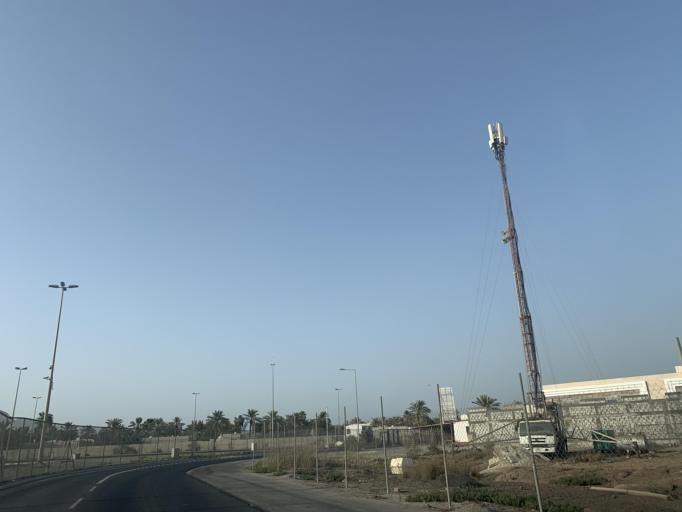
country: BH
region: Central Governorate
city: Madinat Hamad
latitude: 26.1743
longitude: 50.4526
